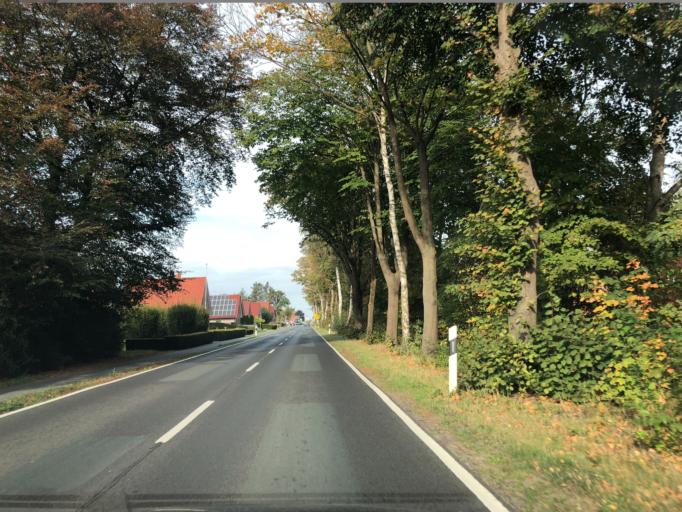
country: DE
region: Lower Saxony
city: Papenburg
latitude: 53.0394
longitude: 7.4680
